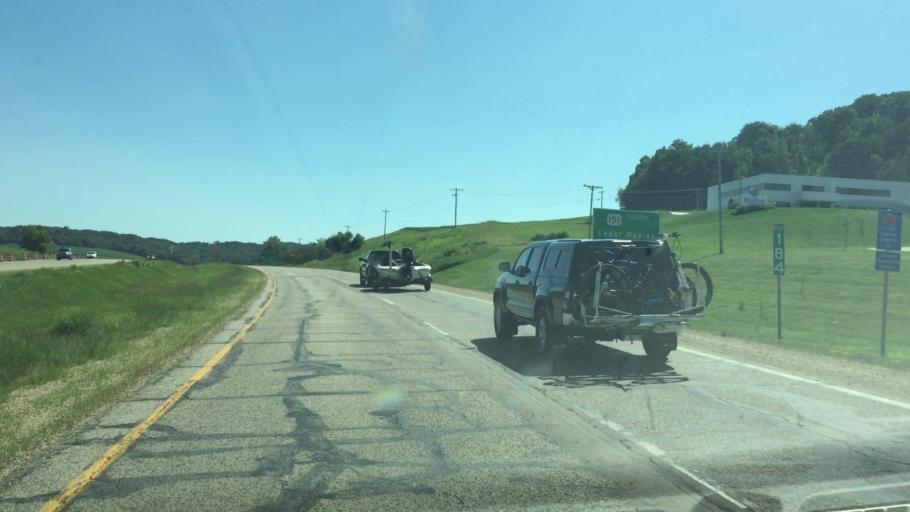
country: US
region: Iowa
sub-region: Dubuque County
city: Dubuque
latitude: 42.4272
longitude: -90.6912
